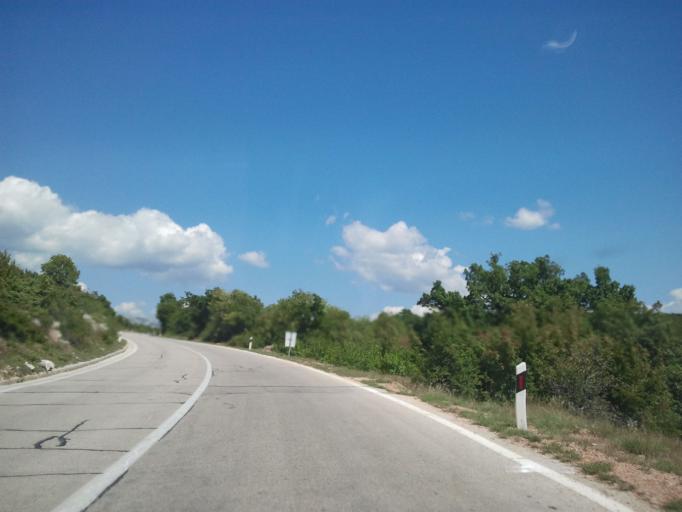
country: HR
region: Zadarska
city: Krusevo
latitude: 44.1861
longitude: 15.6356
